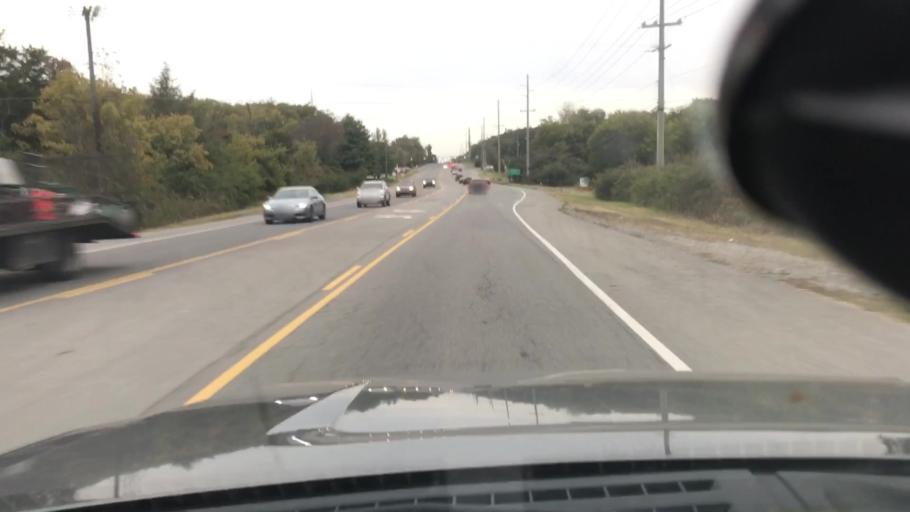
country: US
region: Tennessee
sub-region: Davidson County
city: Forest Hills
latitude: 36.0438
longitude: -86.8657
